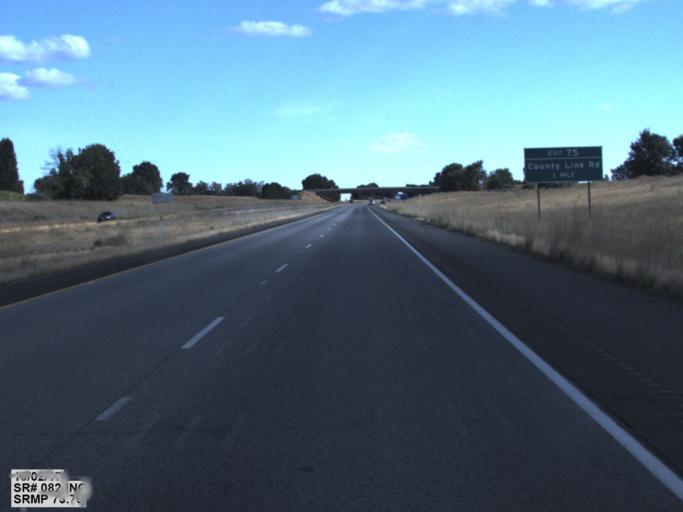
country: US
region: Washington
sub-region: Yakima County
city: Grandview
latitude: 46.2655
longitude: -119.9015
